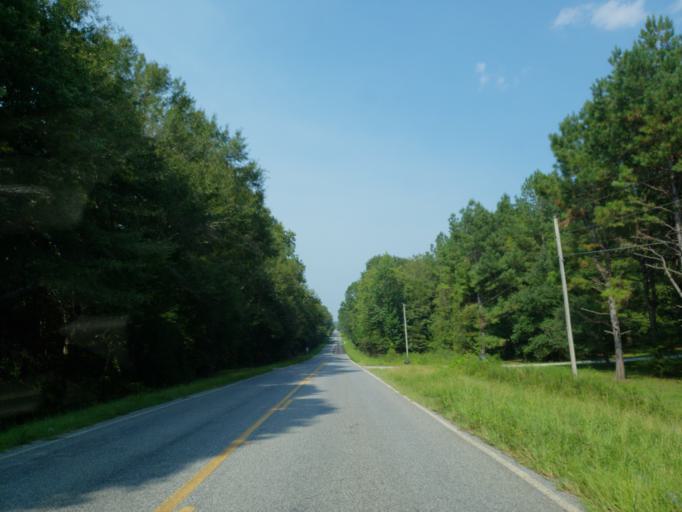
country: US
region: Mississippi
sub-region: Jones County
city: Sharon
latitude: 31.8705
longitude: -88.9682
